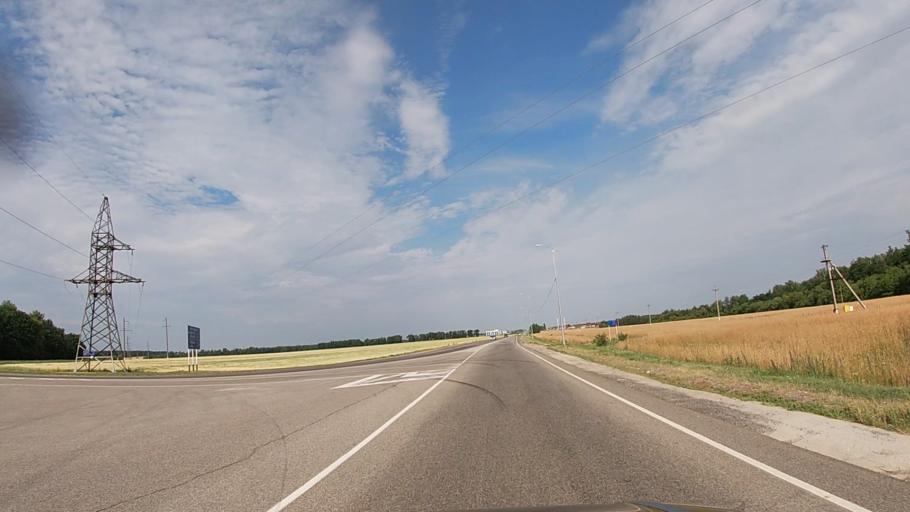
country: RU
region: Belgorod
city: Krasnaya Yaruga
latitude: 50.7962
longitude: 35.7100
